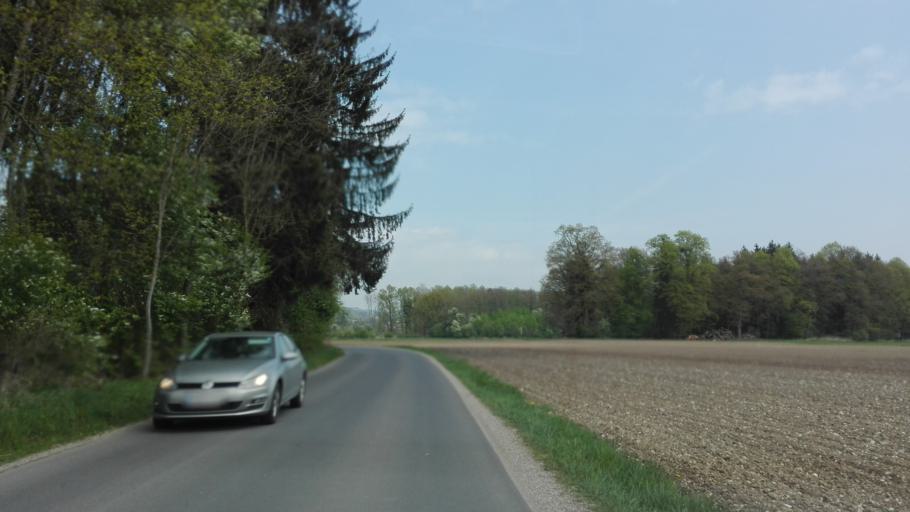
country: AT
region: Upper Austria
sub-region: Politischer Bezirk Perg
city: Perg
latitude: 48.2124
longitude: 14.6927
